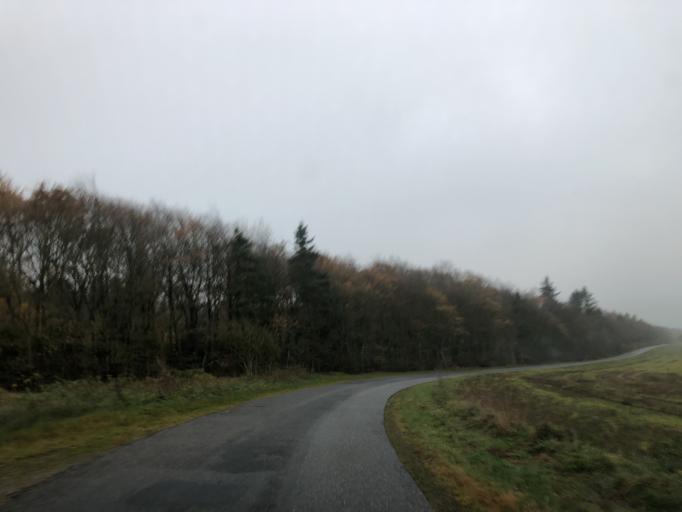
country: DK
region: Central Jutland
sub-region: Herning Kommune
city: Vildbjerg
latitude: 56.2010
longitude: 8.6706
